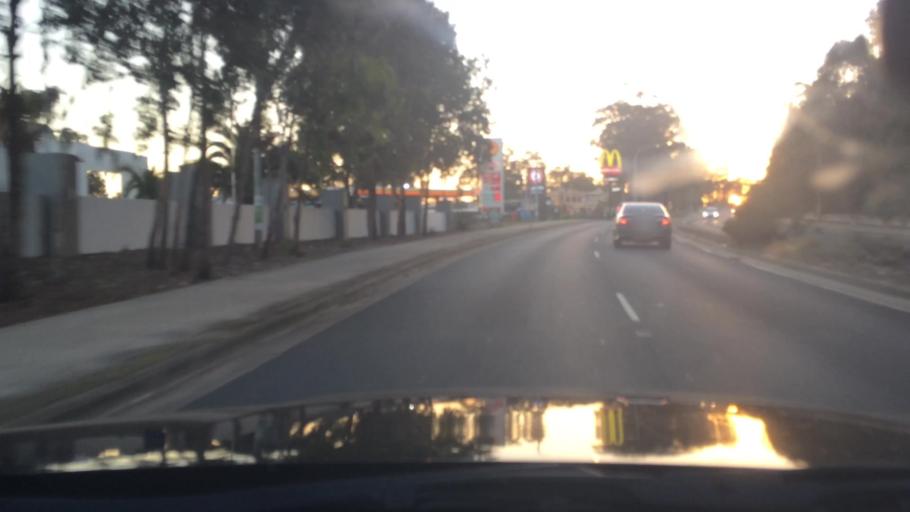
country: AU
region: New South Wales
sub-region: Fairfield
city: Fairfield Heights
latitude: -33.8505
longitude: 150.9001
